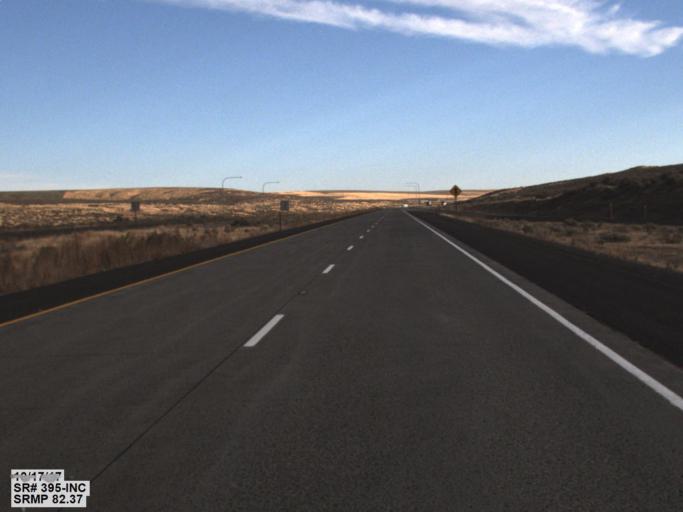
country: US
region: Washington
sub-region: Adams County
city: Ritzville
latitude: 46.9729
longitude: -118.5669
